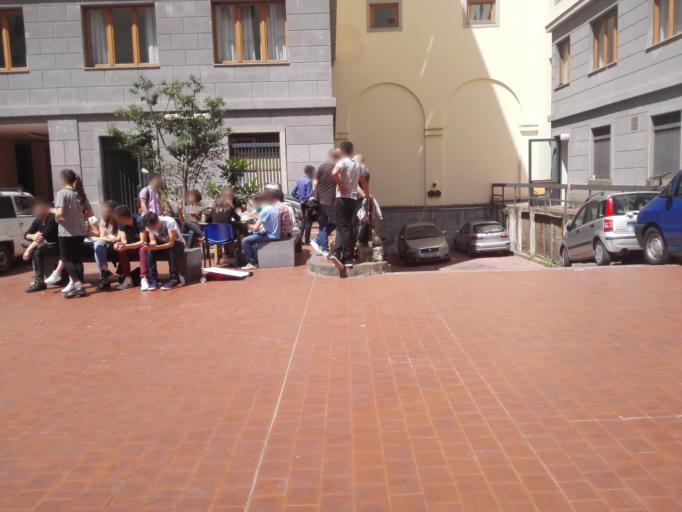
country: IT
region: Campania
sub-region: Provincia di Napoli
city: Napoli
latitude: 40.8469
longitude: 14.2483
